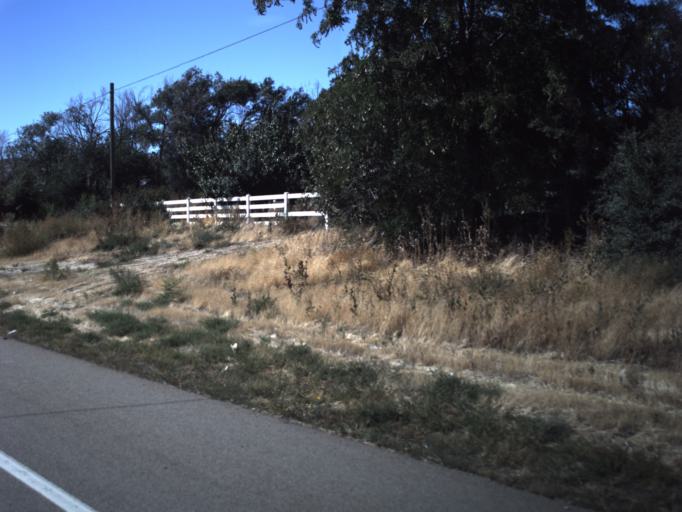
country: US
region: Utah
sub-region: Salt Lake County
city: Bluffdale
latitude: 40.4764
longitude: -111.9460
